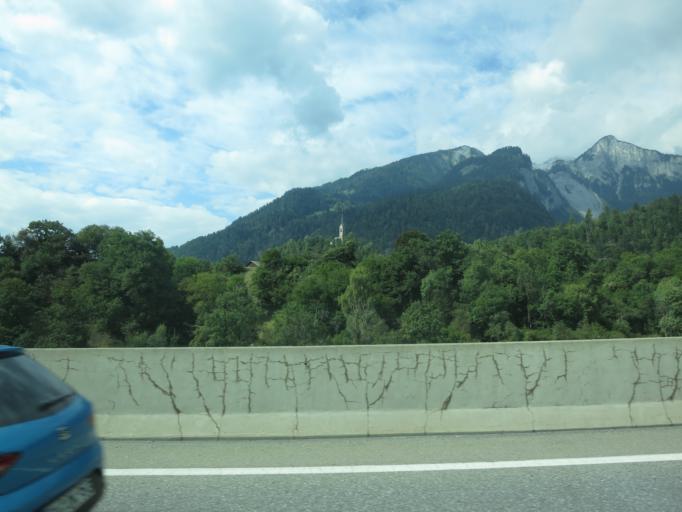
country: CH
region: Grisons
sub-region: Imboden District
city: Tamins
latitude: 46.8267
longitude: 9.4154
